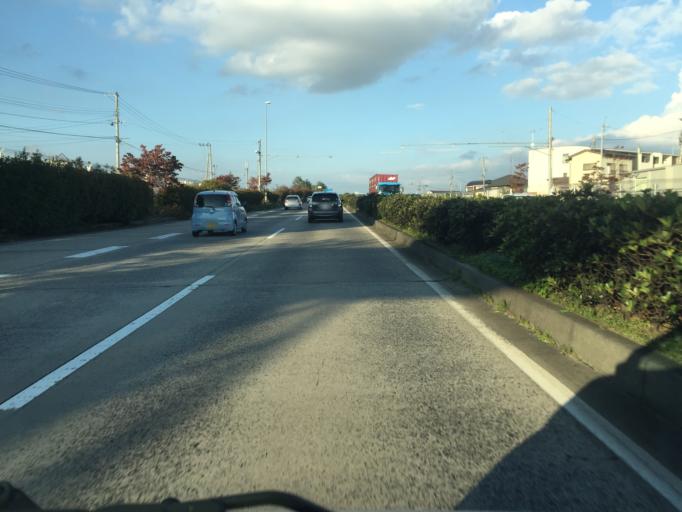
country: JP
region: Fukushima
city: Koriyama
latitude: 37.4238
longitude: 140.3574
